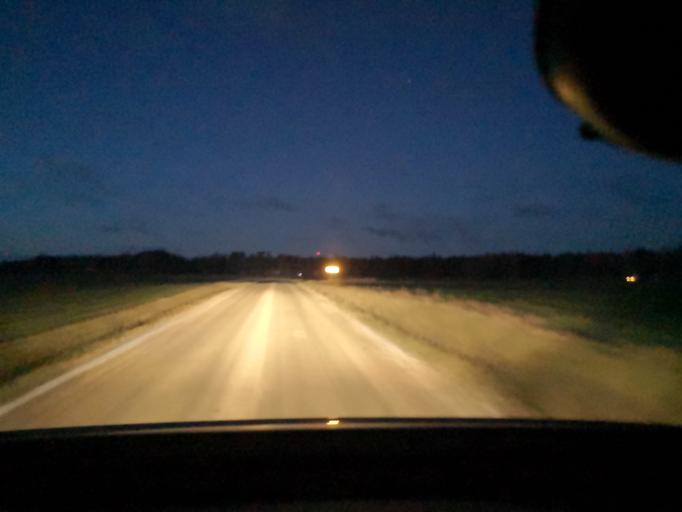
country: SE
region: Uppsala
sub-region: Heby Kommun
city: Heby
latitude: 59.9279
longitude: 16.7553
